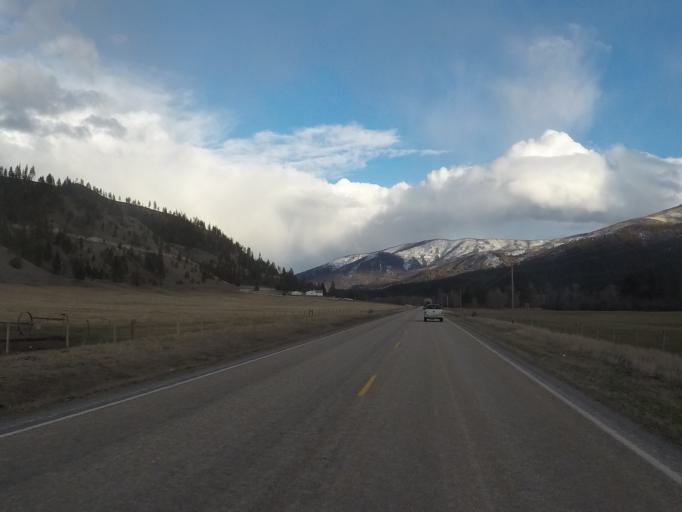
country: US
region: Montana
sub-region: Missoula County
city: Lolo
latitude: 46.7622
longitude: -114.2624
